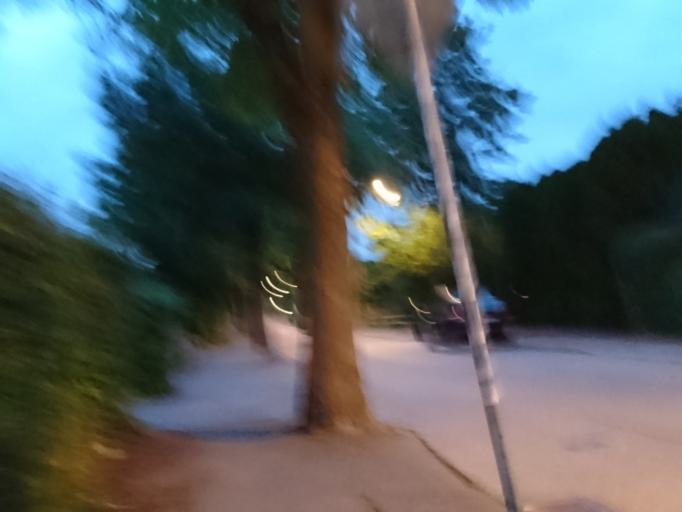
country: SE
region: Stockholm
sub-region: Huddinge Kommun
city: Huddinge
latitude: 59.2760
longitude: 17.9930
